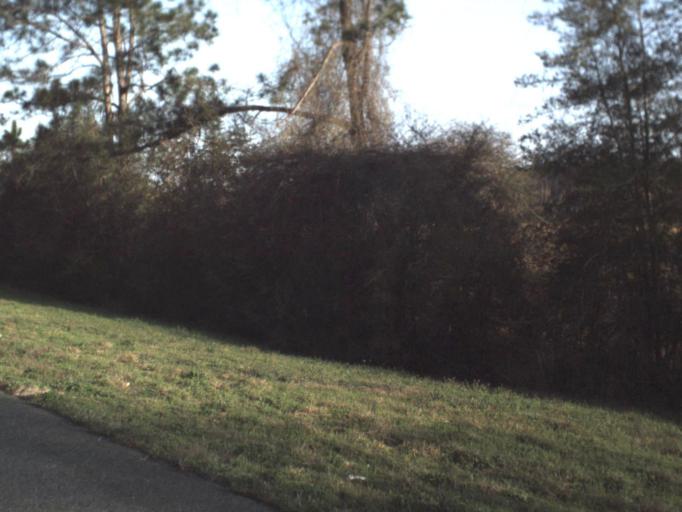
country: US
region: Florida
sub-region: Bay County
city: Lynn Haven
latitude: 30.4395
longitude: -85.7665
